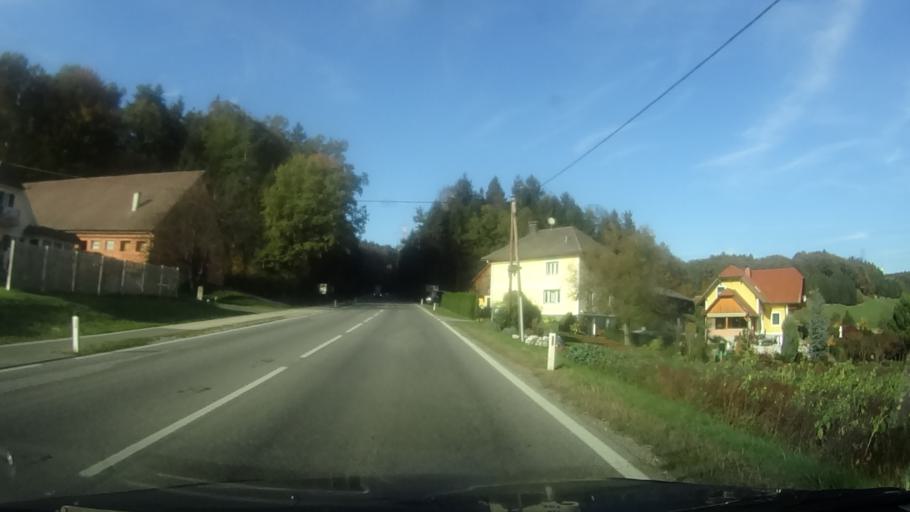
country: AT
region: Styria
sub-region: Politischer Bezirk Leibnitz
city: Weitendorf
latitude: 46.8683
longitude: 15.4775
